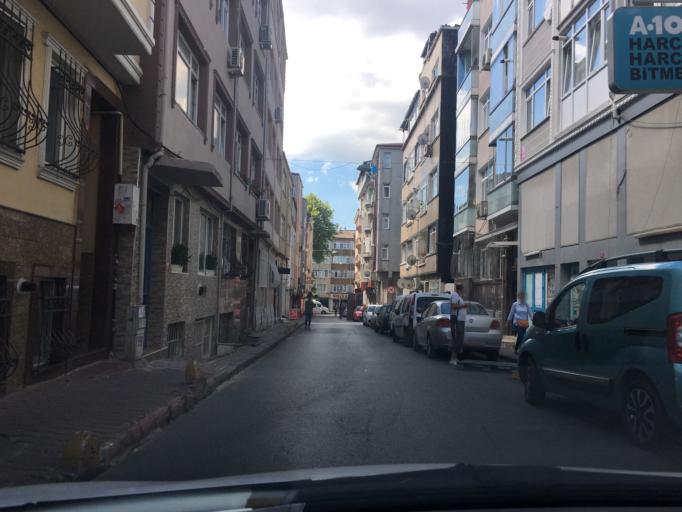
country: TR
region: Istanbul
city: Istanbul
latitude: 41.0078
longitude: 28.9334
